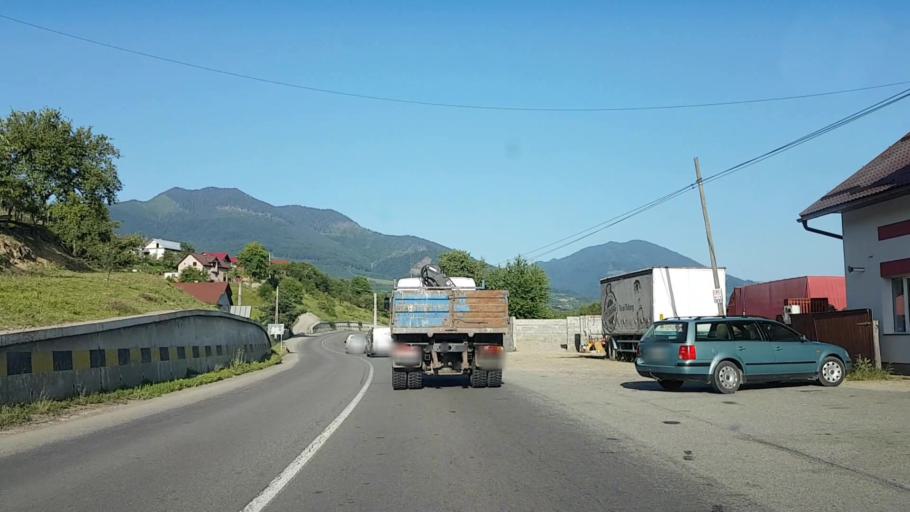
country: RO
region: Bistrita-Nasaud
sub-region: Comuna Tiha Bargaului
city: Tureac
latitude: 47.2298
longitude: 24.7977
